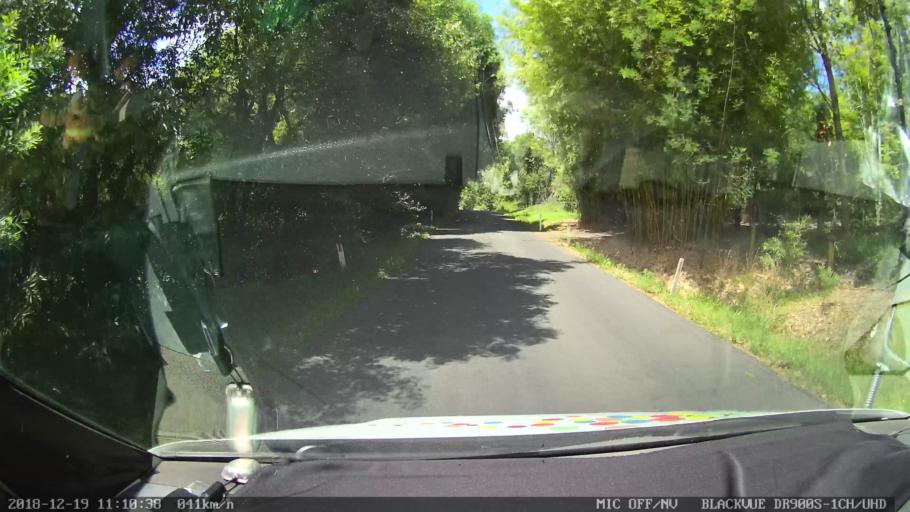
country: AU
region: New South Wales
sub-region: Lismore Municipality
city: Nimbin
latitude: -28.6391
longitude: 153.2601
